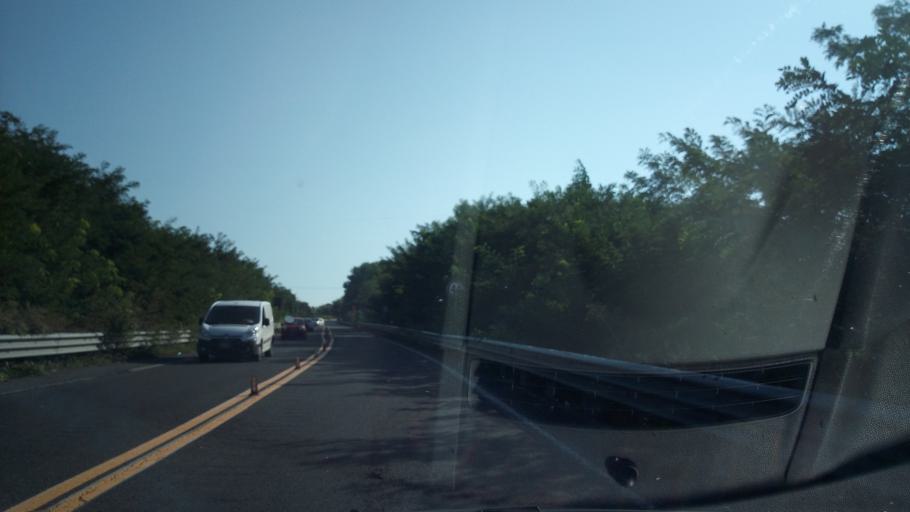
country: IT
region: Campania
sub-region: Provincia di Avellino
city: San Potito Ultra
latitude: 40.9315
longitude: 14.8725
